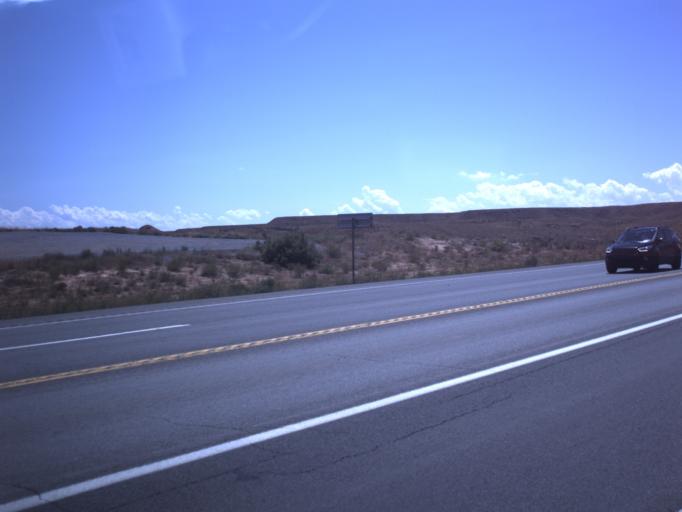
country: US
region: Utah
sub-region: Uintah County
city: Maeser
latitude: 40.3187
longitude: -109.6952
